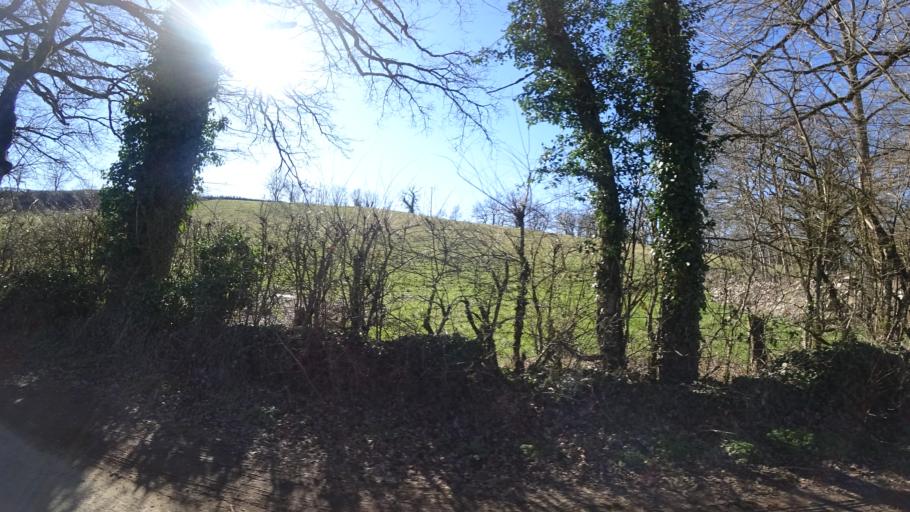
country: FR
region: Midi-Pyrenees
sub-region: Departement de l'Aveyron
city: Sebazac-Concoures
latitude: 44.4067
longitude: 2.5628
